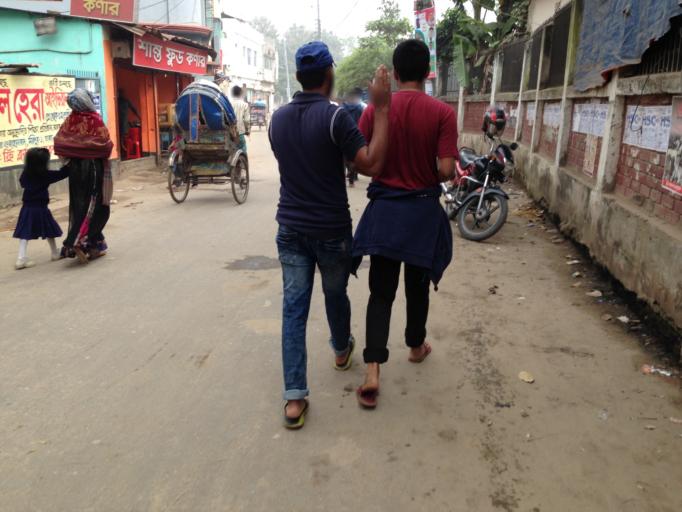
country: BD
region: Dhaka
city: Azimpur
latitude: 23.7927
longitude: 90.3430
